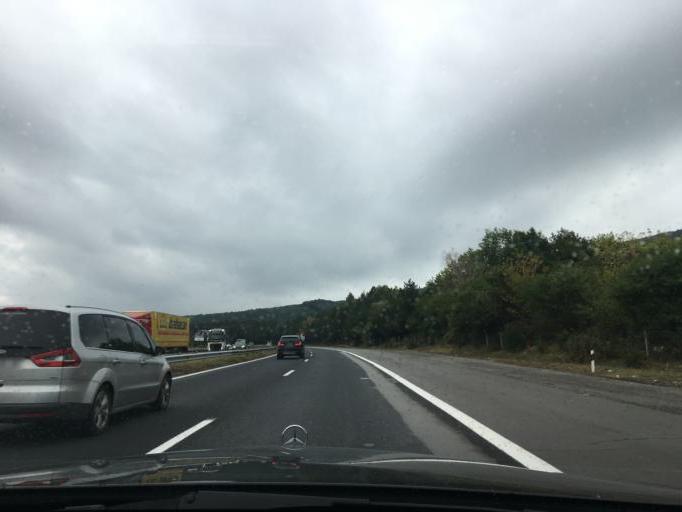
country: BG
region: Sofiya
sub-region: Obshtina Elin Pelin
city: Elin Pelin
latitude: 42.5993
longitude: 23.5671
